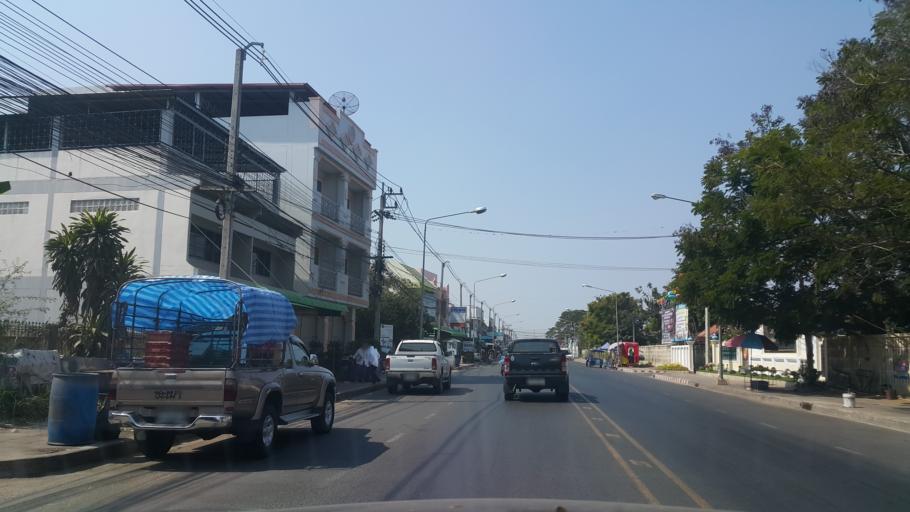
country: TH
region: Buriram
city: Satuek
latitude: 15.2947
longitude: 103.2901
